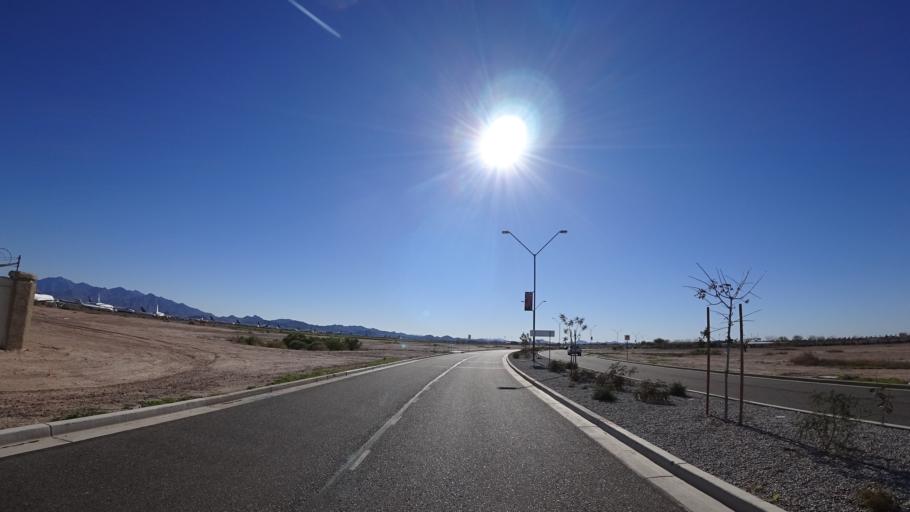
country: US
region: Arizona
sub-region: Maricopa County
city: Goodyear
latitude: 33.4340
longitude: -112.3761
